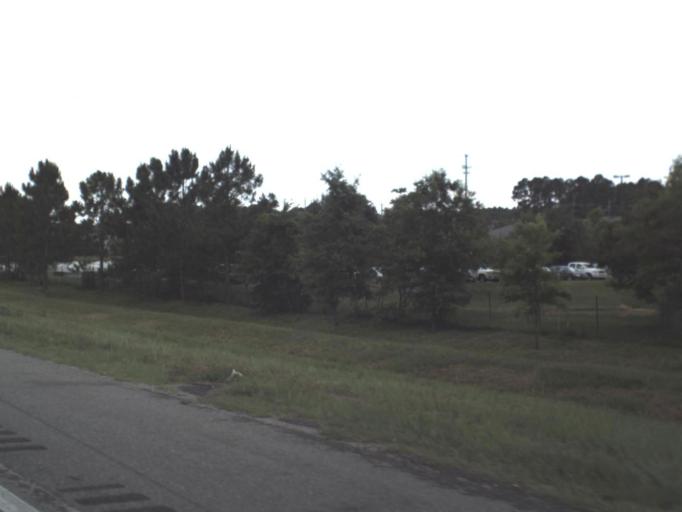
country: US
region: Florida
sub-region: Duval County
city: Neptune Beach
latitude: 30.3050
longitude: -81.5238
